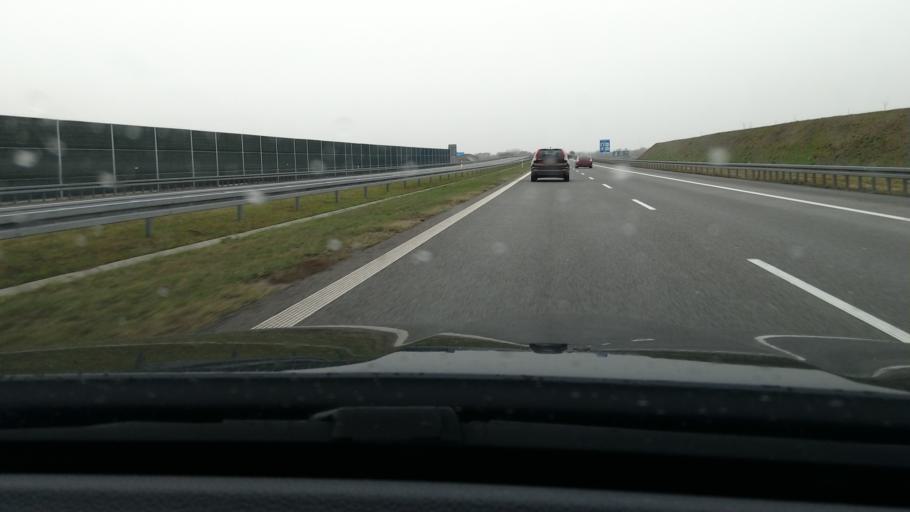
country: PL
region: Masovian Voivodeship
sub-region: Powiat warszawski zachodni
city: Bieniewice
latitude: 52.1287
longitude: 20.5378
